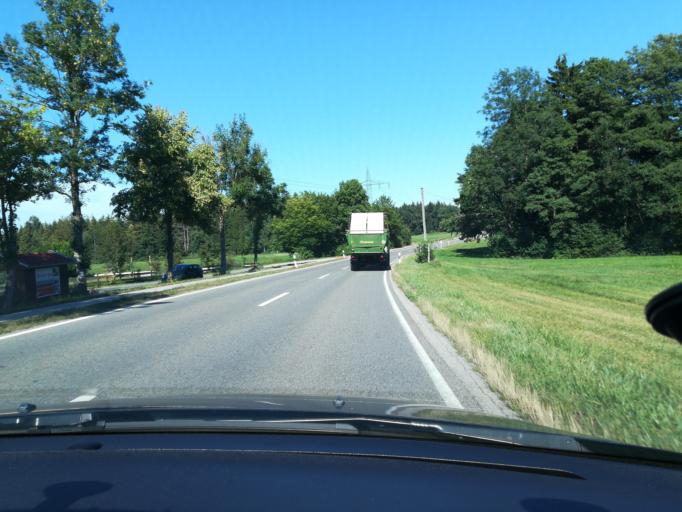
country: DE
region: Bavaria
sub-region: Upper Bavaria
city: Gstadt am Chiemsee
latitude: 47.9221
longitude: 12.4225
